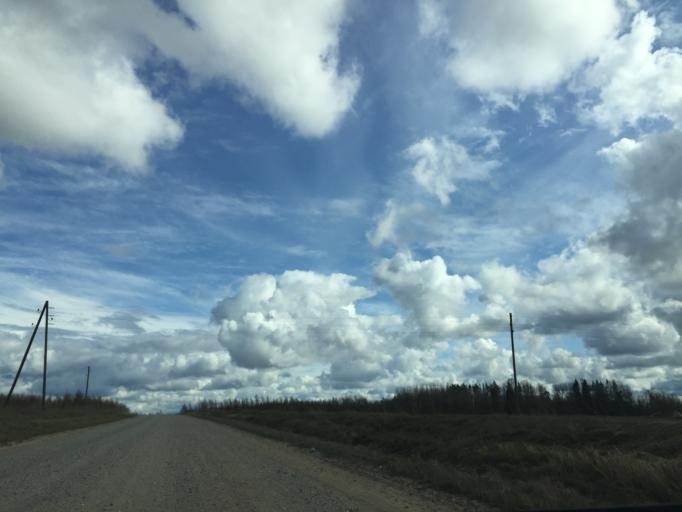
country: LV
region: Limbazu Rajons
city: Limbazi
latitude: 57.6058
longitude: 24.7965
